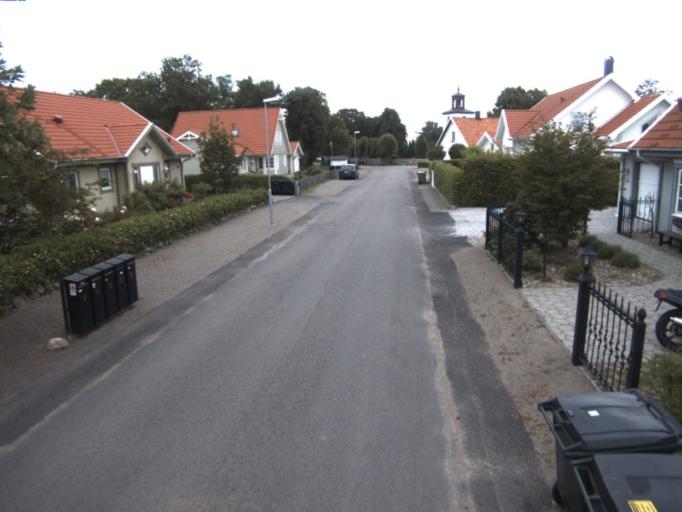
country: SE
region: Skane
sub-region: Angelholms Kommun
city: Strovelstorp
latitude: 56.1107
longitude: 12.7888
